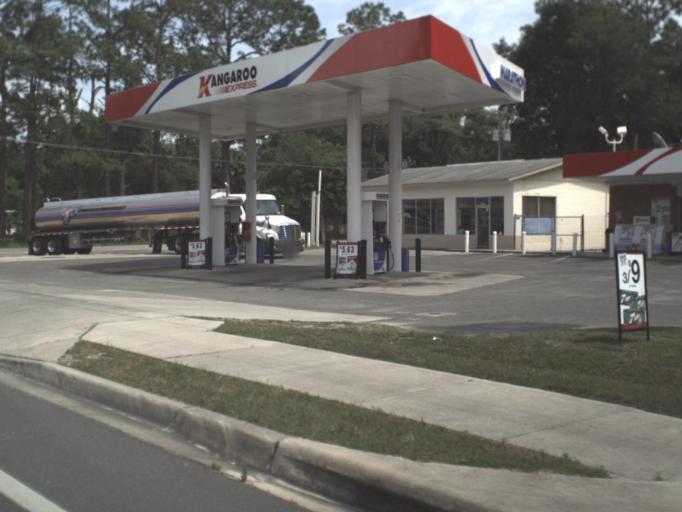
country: US
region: Florida
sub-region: Putnam County
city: Interlachen
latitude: 29.6277
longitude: -81.8456
